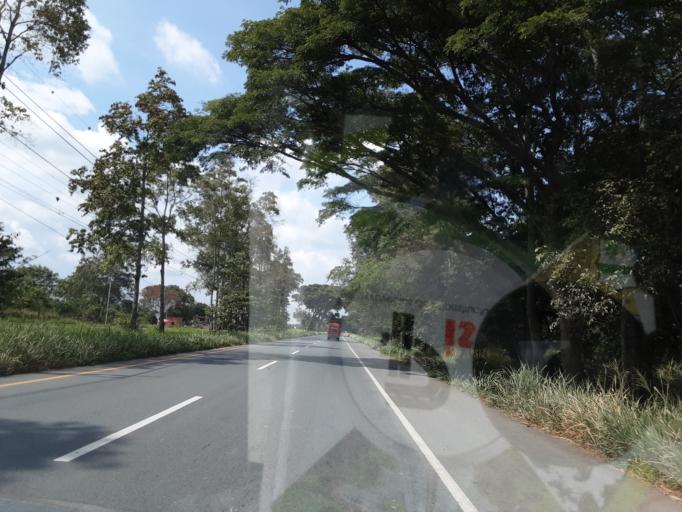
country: CO
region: Valle del Cauca
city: Guacari
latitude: 3.7477
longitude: -76.3251
